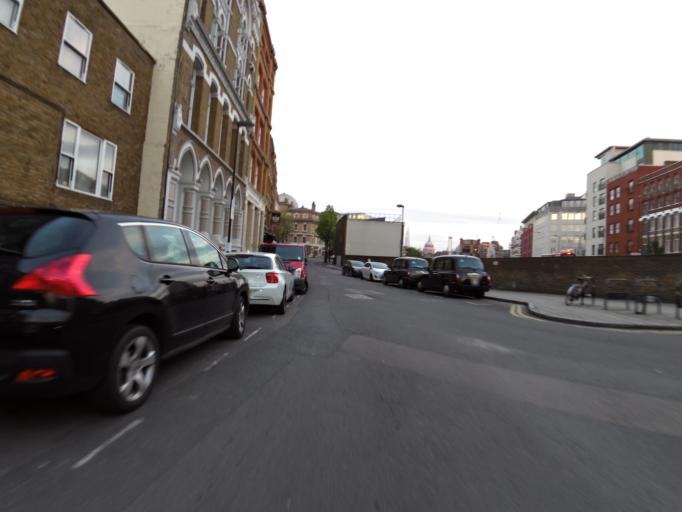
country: GB
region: England
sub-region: Greater London
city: Clerkenwell
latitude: 51.5232
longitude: -0.1076
